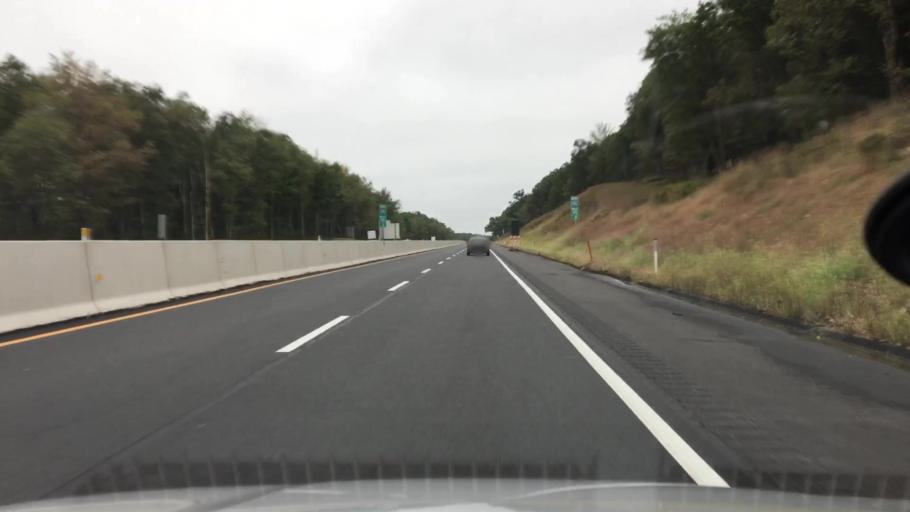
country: US
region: Pennsylvania
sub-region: Luzerne County
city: White Haven
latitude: 41.0746
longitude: -75.7111
